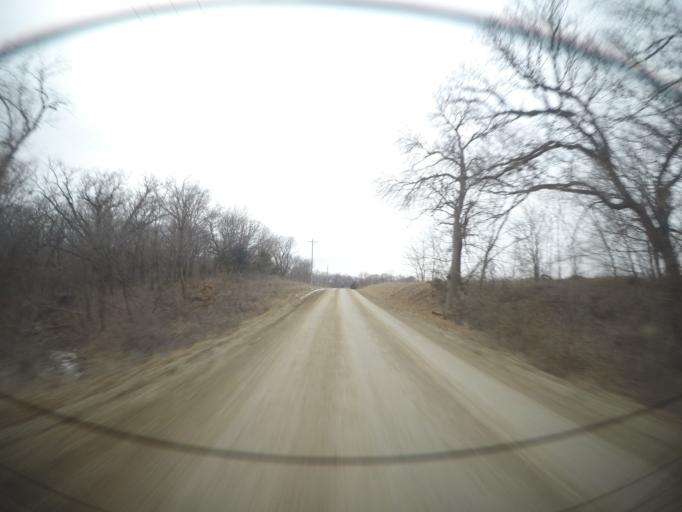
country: US
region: Kansas
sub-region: Pottawatomie County
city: Wamego
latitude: 39.1523
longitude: -96.2860
